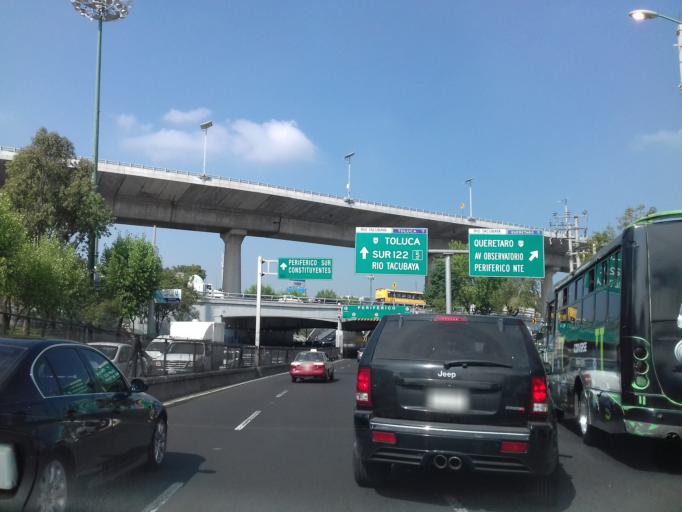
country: MX
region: Mexico City
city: Polanco
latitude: 19.3997
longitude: -99.1898
